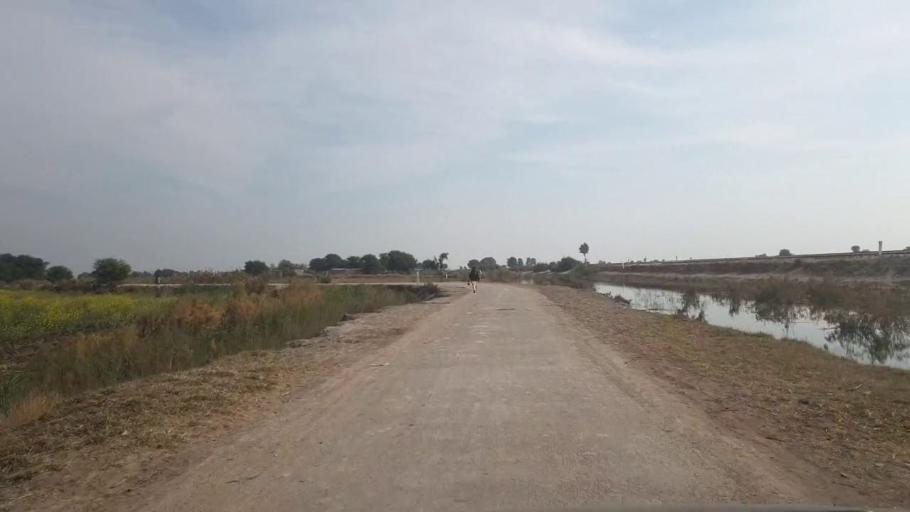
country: PK
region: Sindh
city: Shahpur Chakar
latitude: 26.0803
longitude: 68.4941
